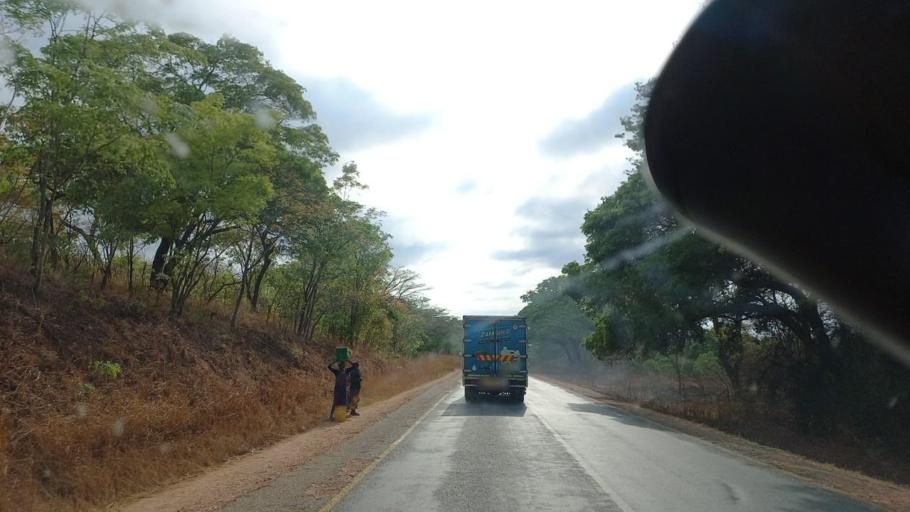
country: ZM
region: Lusaka
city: Chongwe
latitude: -15.2708
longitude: 28.8975
